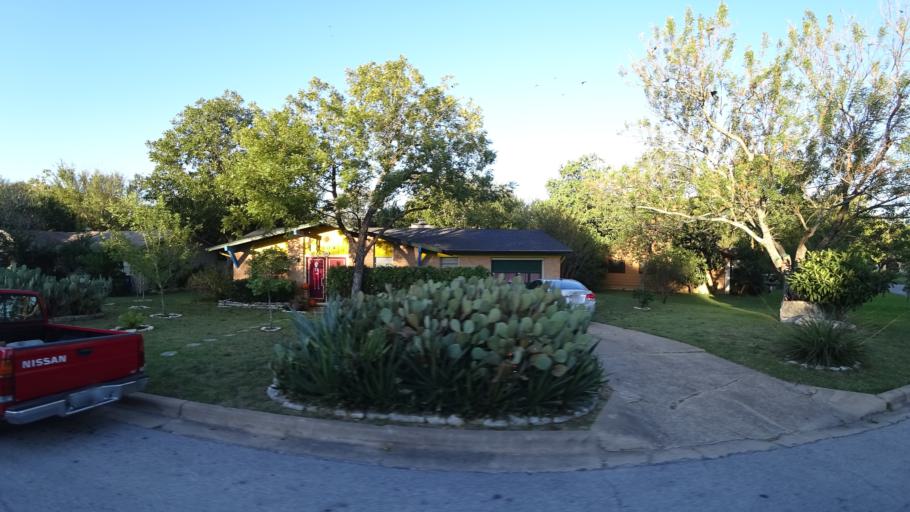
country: US
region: Texas
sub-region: Travis County
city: Austin
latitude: 30.2970
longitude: -97.6795
